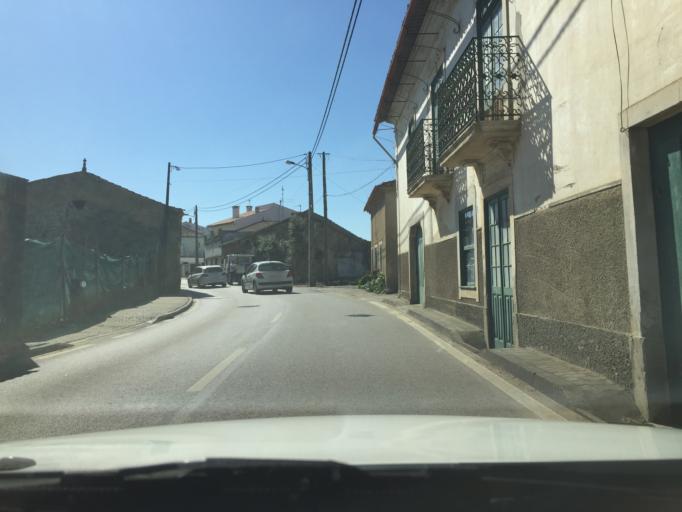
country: PT
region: Aveiro
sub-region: Anadia
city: Sangalhos
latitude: 40.4209
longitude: -8.5291
